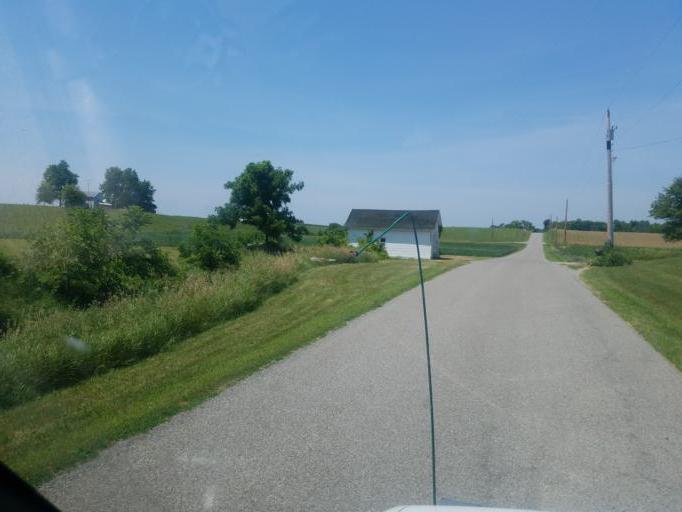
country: US
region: Ohio
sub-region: Logan County
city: West Liberty
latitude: 40.2924
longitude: -83.8277
